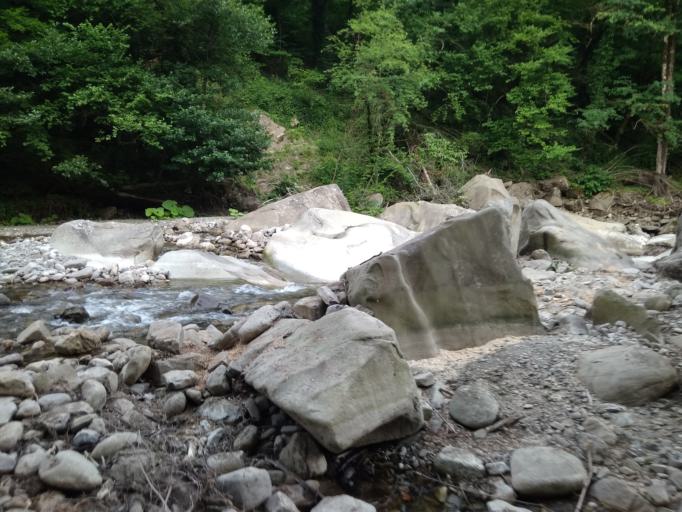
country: RU
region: Krasnodarskiy
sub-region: Sochi City
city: Lazarevskoye
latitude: 44.0031
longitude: 39.4054
